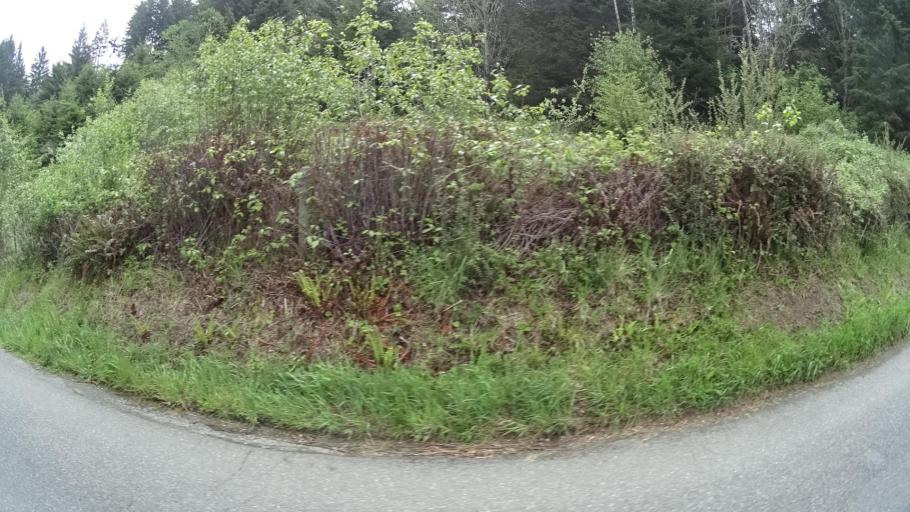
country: US
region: California
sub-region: Humboldt County
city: Bayside
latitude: 40.8422
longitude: -124.0244
